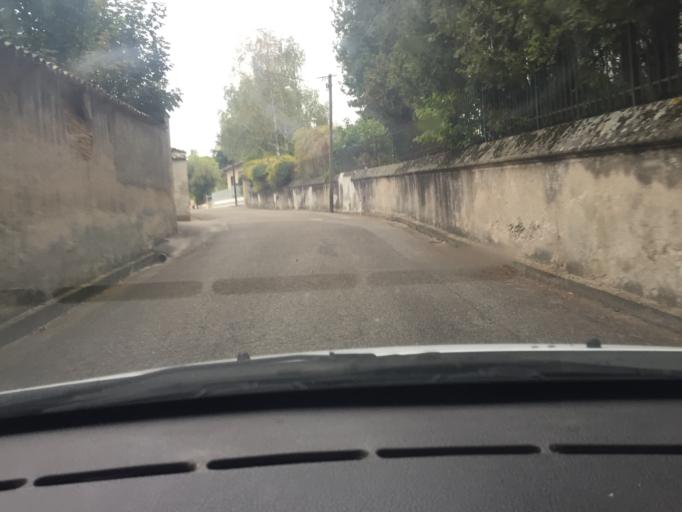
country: FR
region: Rhone-Alpes
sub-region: Departement du Rhone
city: Rillieux-la-Pape
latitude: 45.8048
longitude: 4.8809
